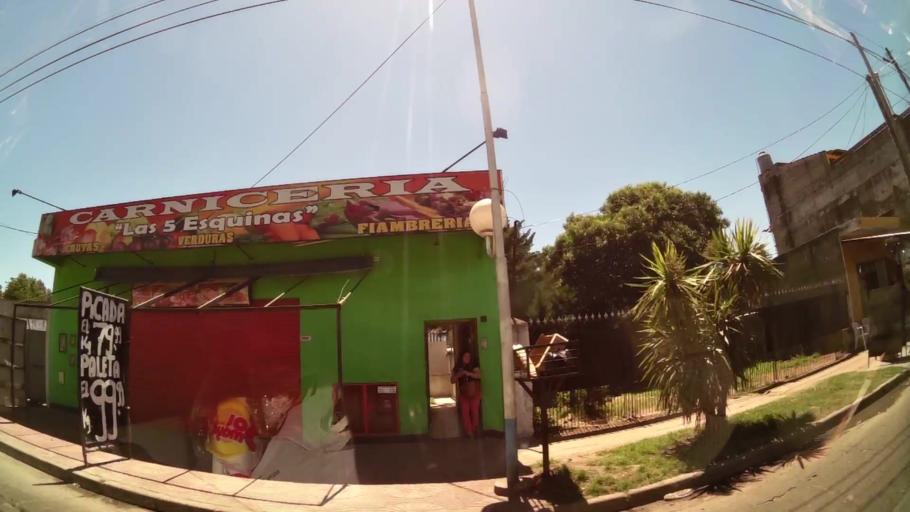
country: AR
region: Buenos Aires
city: Hurlingham
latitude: -34.5024
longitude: -58.6816
